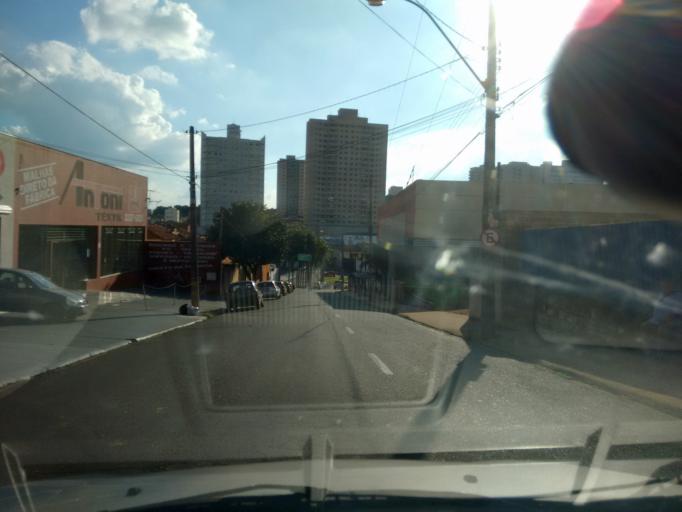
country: BR
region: Sao Paulo
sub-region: Araraquara
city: Araraquara
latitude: -21.7970
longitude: -48.1714
